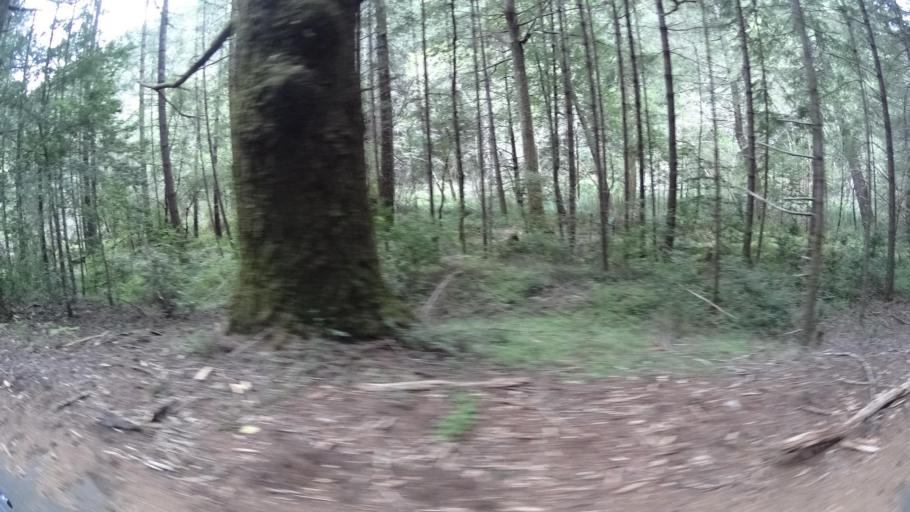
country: US
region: California
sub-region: Humboldt County
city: Redway
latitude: 40.0200
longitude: -124.0043
